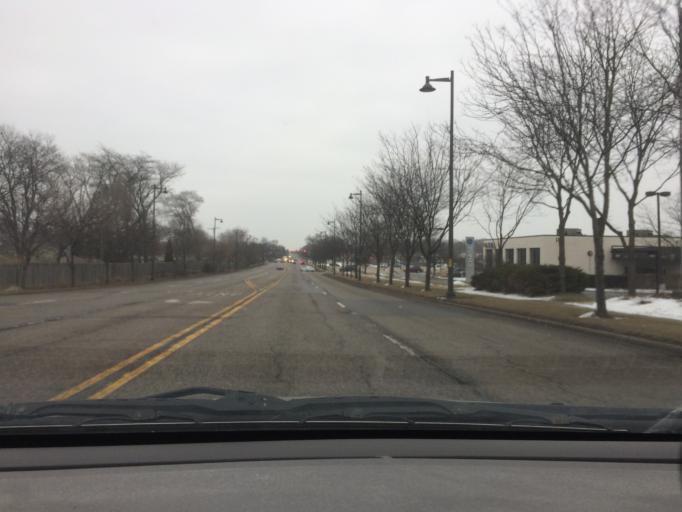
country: US
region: Illinois
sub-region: Cook County
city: Streamwood
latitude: 42.0129
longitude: -88.1798
